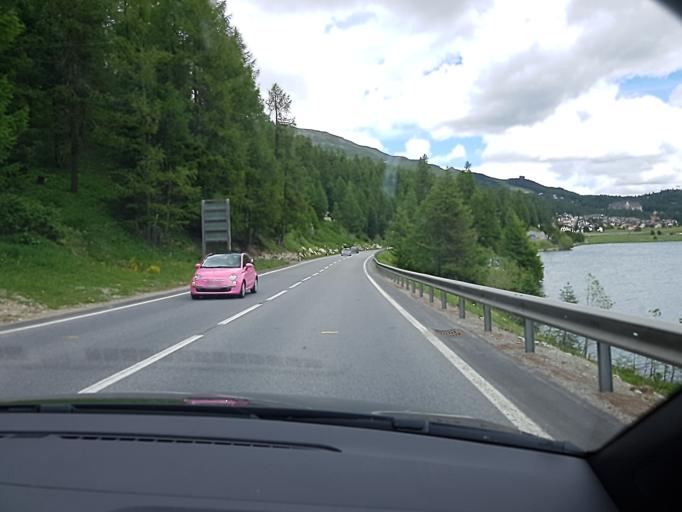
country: CH
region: Grisons
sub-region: Maloja District
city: Silvaplana
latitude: 46.4688
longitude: 9.8023
